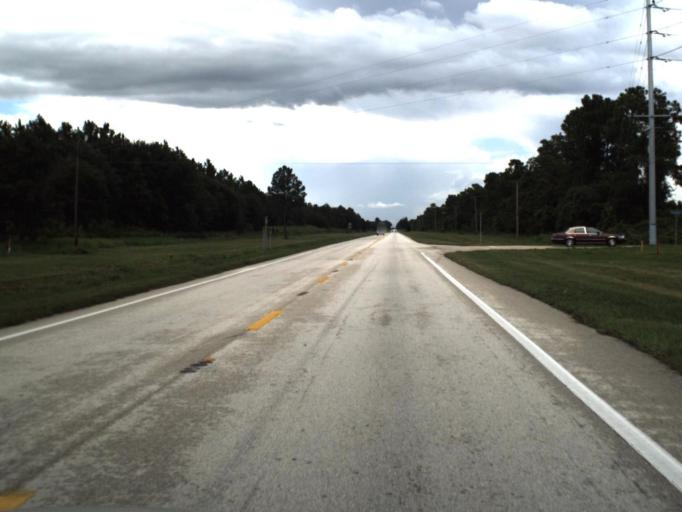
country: US
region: Florida
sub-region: Polk County
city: Mulberry
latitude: 27.8209
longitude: -81.9806
